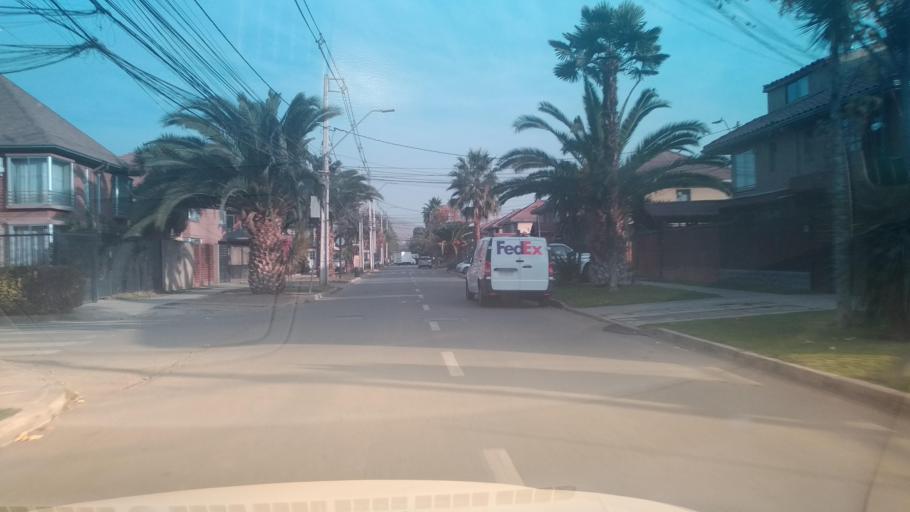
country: CL
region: Santiago Metropolitan
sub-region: Provincia de Santiago
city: Lo Prado
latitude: -33.3582
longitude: -70.7137
